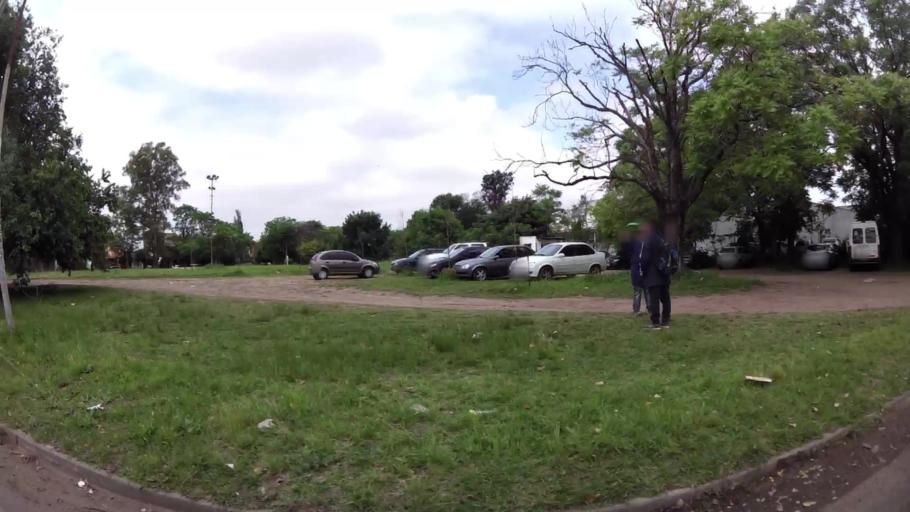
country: AR
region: Buenos Aires
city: San Justo
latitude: -34.7298
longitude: -58.5348
